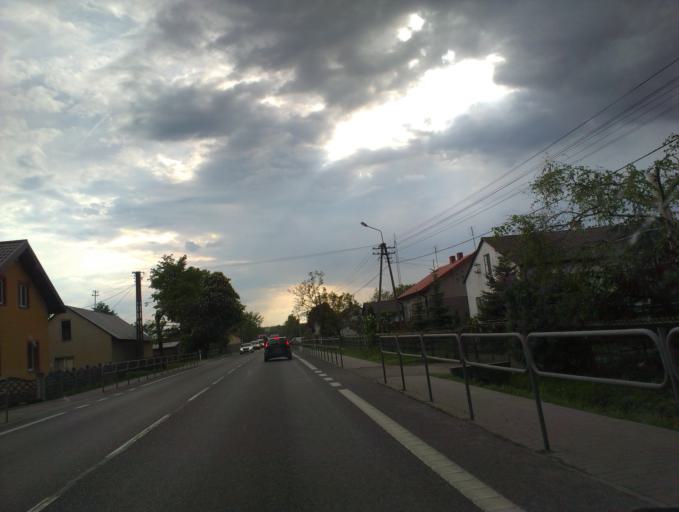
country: PL
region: Masovian Voivodeship
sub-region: Powiat grojecki
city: Pniewy
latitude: 51.9122
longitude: 20.7114
